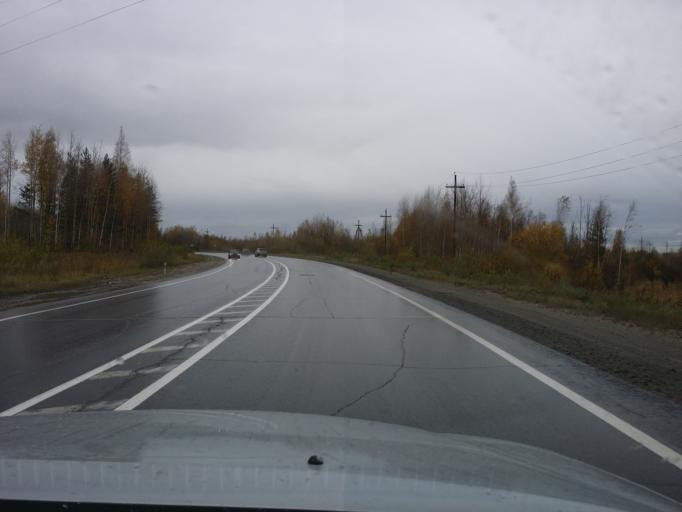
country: RU
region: Khanty-Mansiyskiy Avtonomnyy Okrug
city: Megion
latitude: 61.0840
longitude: 76.1167
